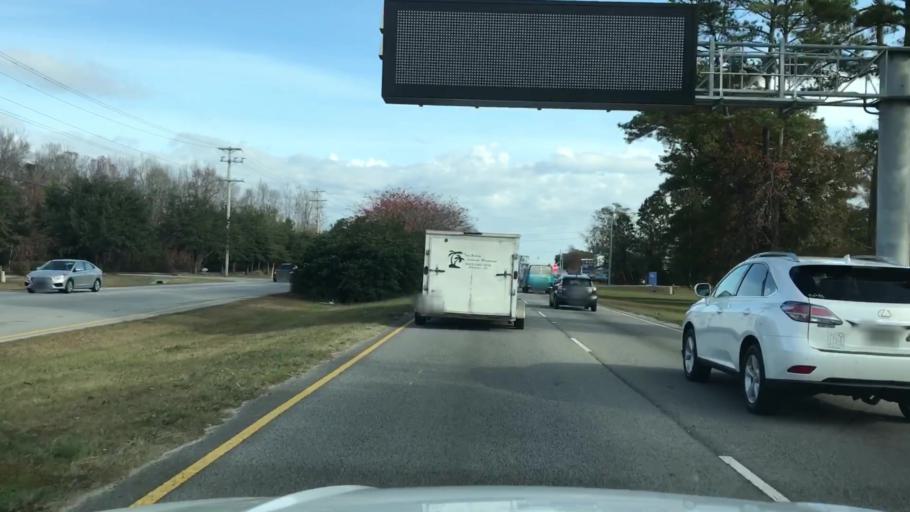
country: US
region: South Carolina
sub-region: Georgetown County
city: Murrells Inlet
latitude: 33.5565
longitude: -79.0436
